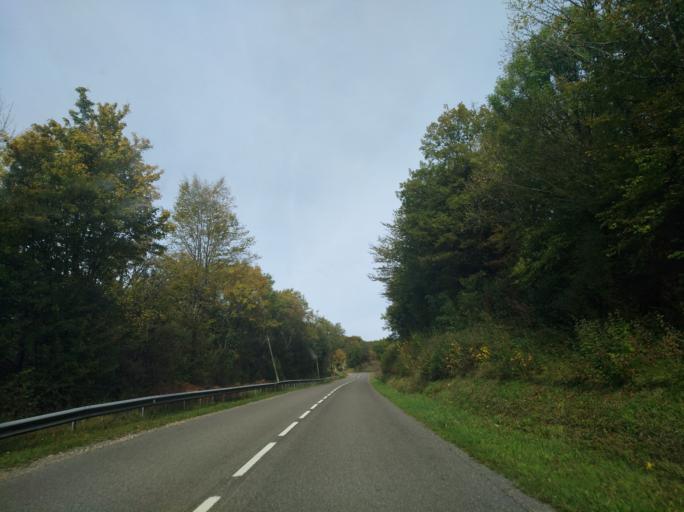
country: FR
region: Bourgogne
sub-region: Departement de Saone-et-Loire
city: Cuiseaux
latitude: 46.4558
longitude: 5.3919
